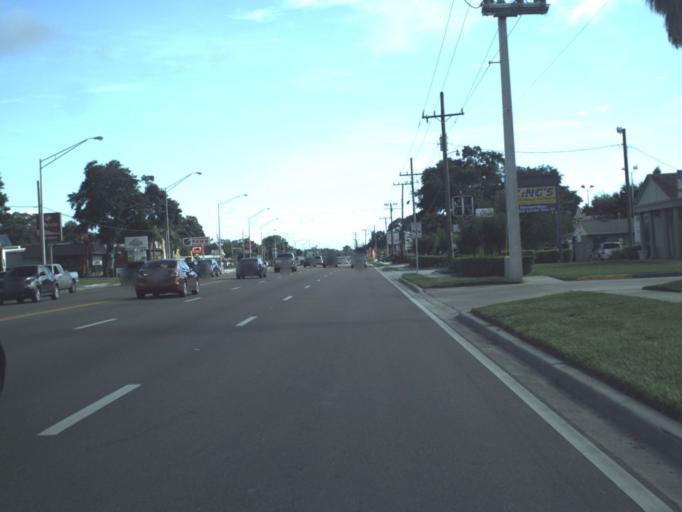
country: US
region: Florida
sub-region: Manatee County
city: West Samoset
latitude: 27.4733
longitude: -82.5631
